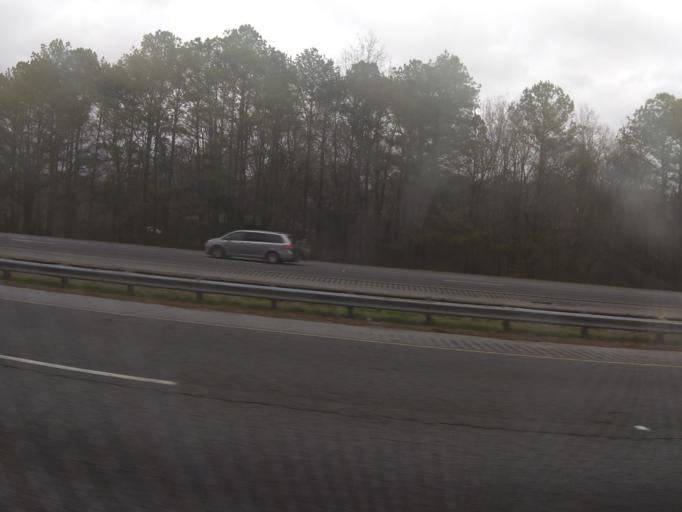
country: US
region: Georgia
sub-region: Gordon County
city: Calhoun
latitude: 34.6203
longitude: -84.9672
